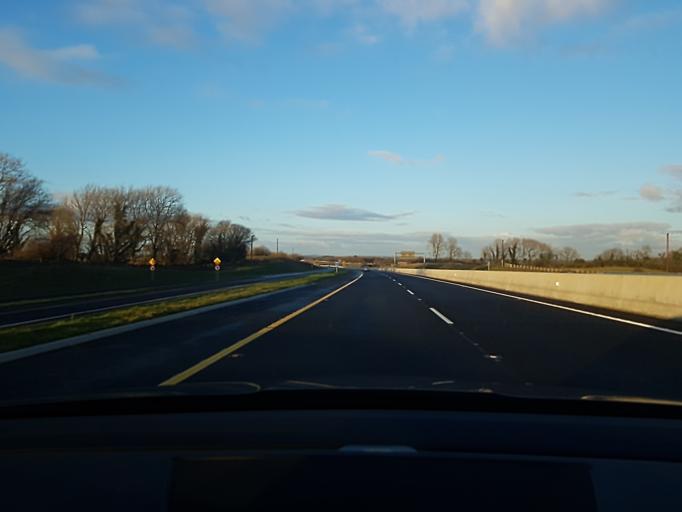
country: IE
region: Connaught
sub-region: County Galway
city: Athenry
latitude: 53.3005
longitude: -8.8051
